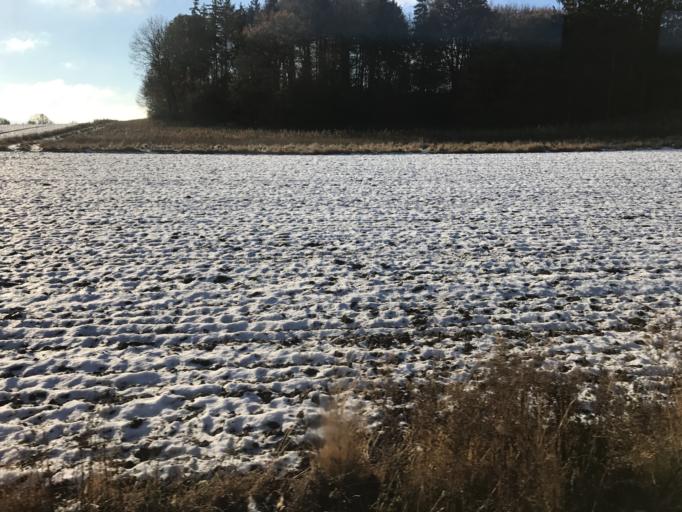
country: DK
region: Zealand
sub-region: Stevns Kommune
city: Store Heddinge
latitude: 55.3493
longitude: 12.3173
